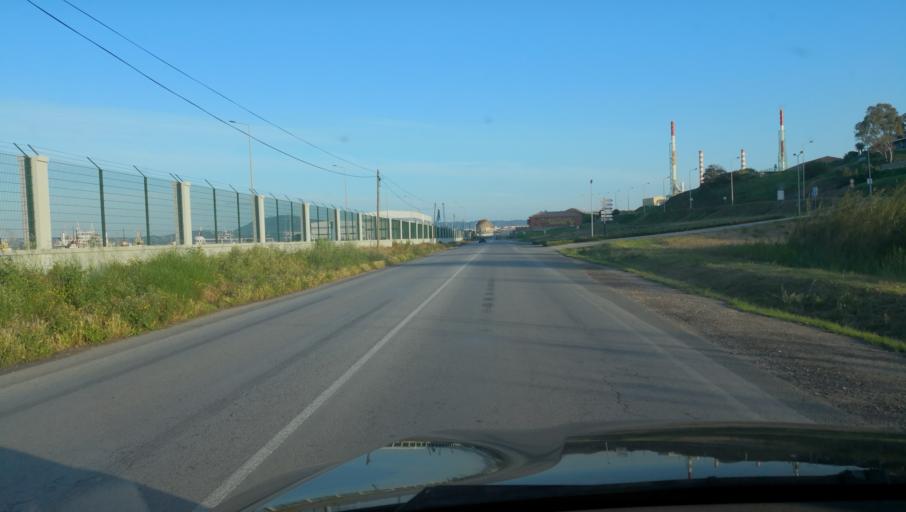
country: PT
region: Setubal
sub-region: Setubal
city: Setubal
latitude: 38.4946
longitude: -8.8325
